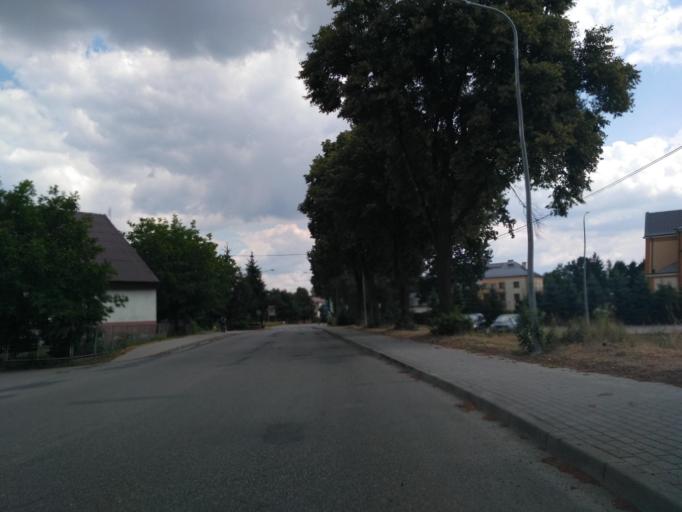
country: PL
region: Subcarpathian Voivodeship
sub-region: Powiat debicki
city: Zyrakow
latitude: 50.0607
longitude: 21.3547
